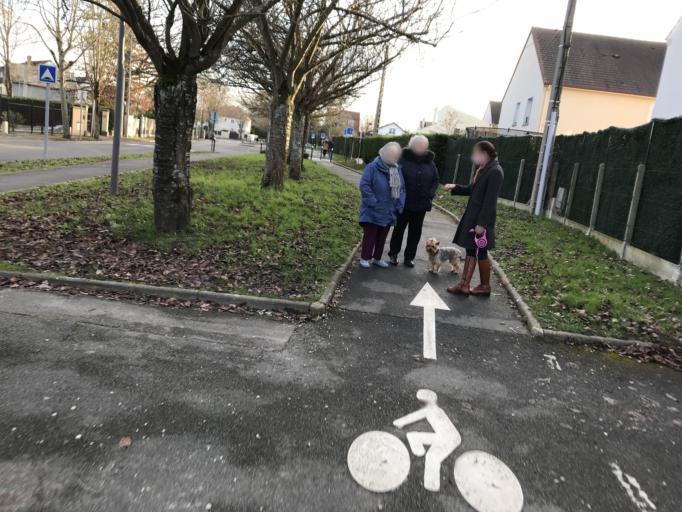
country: FR
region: Ile-de-France
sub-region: Departement de l'Essonne
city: Villebon-sur-Yvette
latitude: 48.7107
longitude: 2.2302
